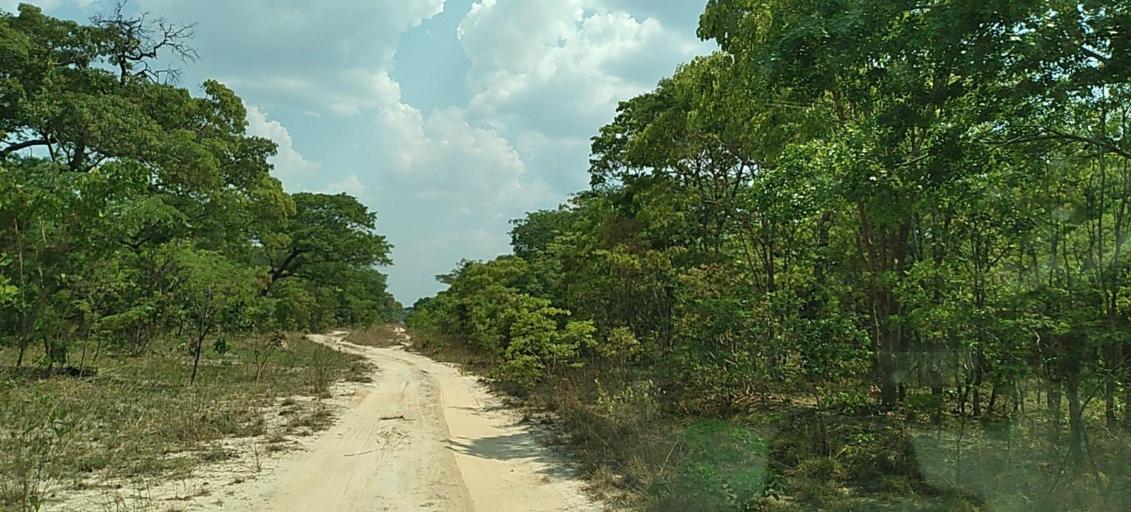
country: ZM
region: Copperbelt
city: Mpongwe
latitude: -13.8282
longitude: 27.9409
